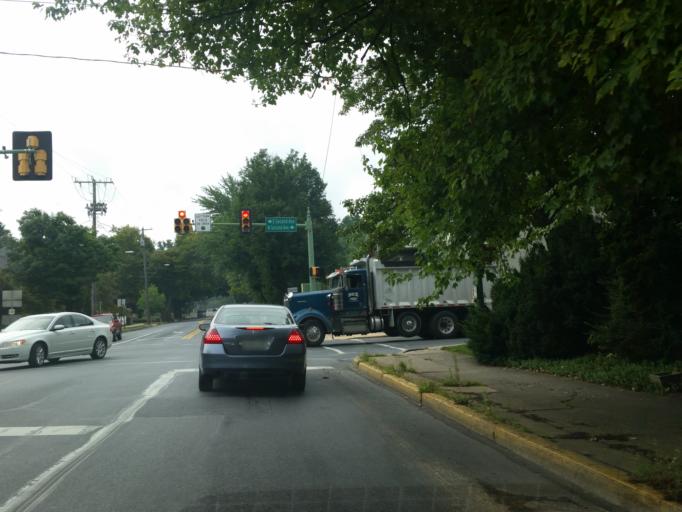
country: US
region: Pennsylvania
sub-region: Lancaster County
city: Lititz
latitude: 40.1504
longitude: -76.3070
